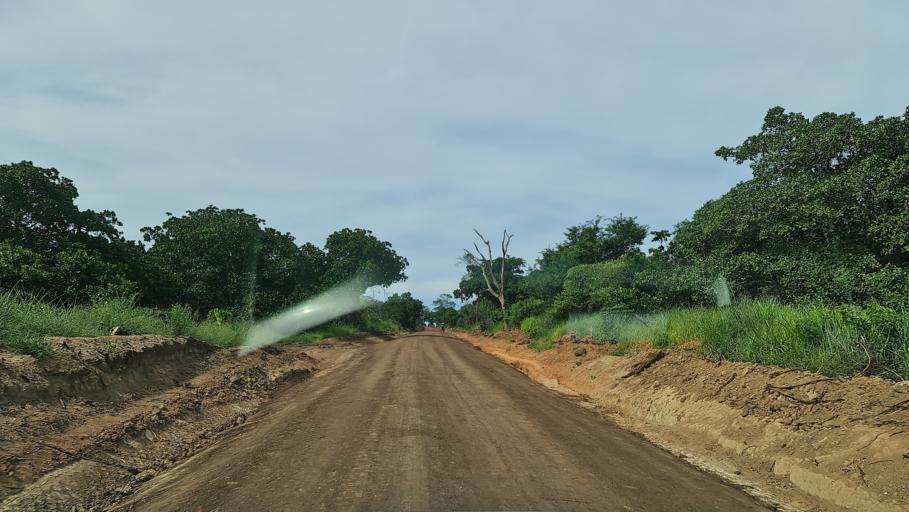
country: MZ
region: Nampula
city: Ilha de Mocambique
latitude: -14.8958
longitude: 40.4665
